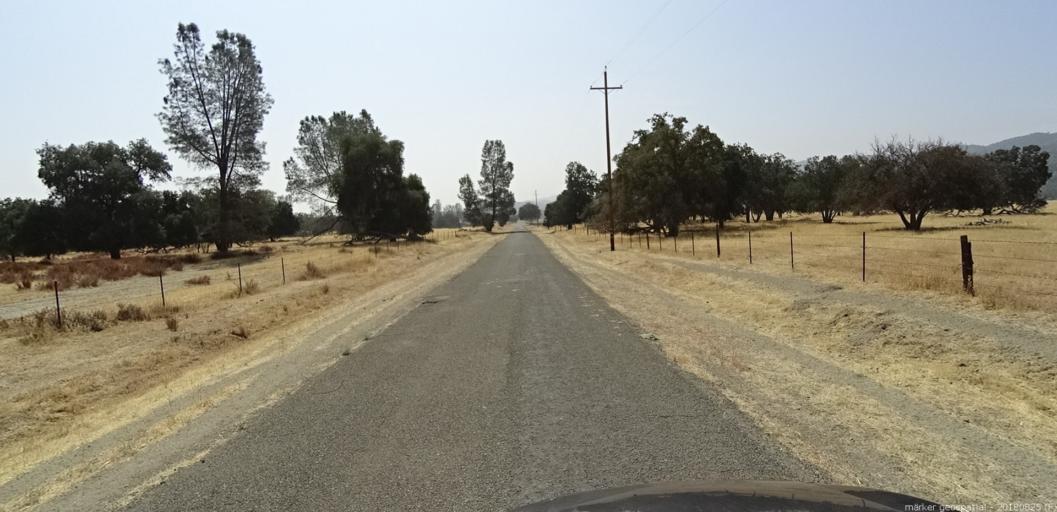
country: US
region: California
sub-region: Fresno County
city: Coalinga
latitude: 35.9434
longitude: -120.5224
